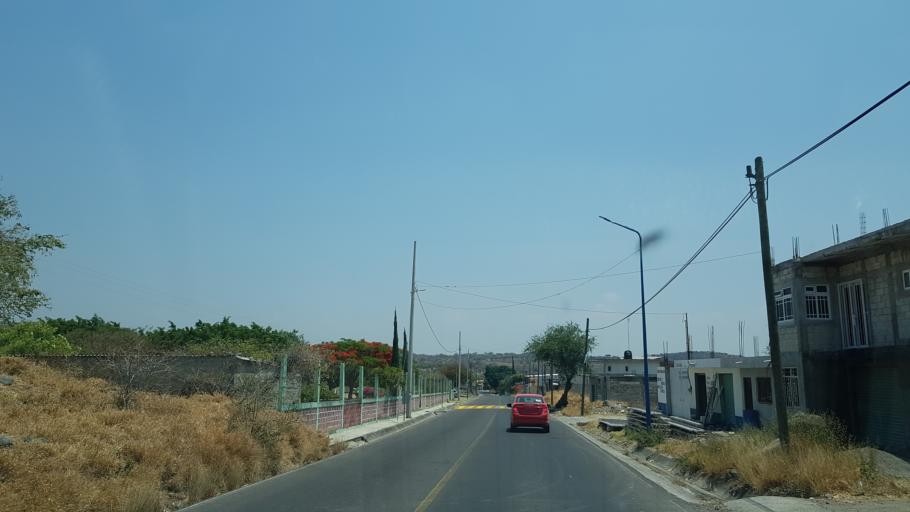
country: MX
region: Puebla
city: Huaquechula
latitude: 18.7639
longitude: -98.5276
